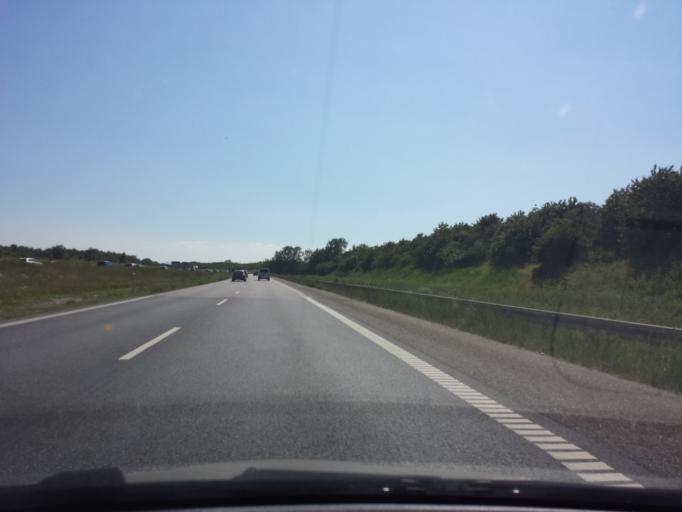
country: DK
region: Capital Region
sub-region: Frederiksberg Kommune
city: Frederiksberg
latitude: 55.6281
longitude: 12.5364
